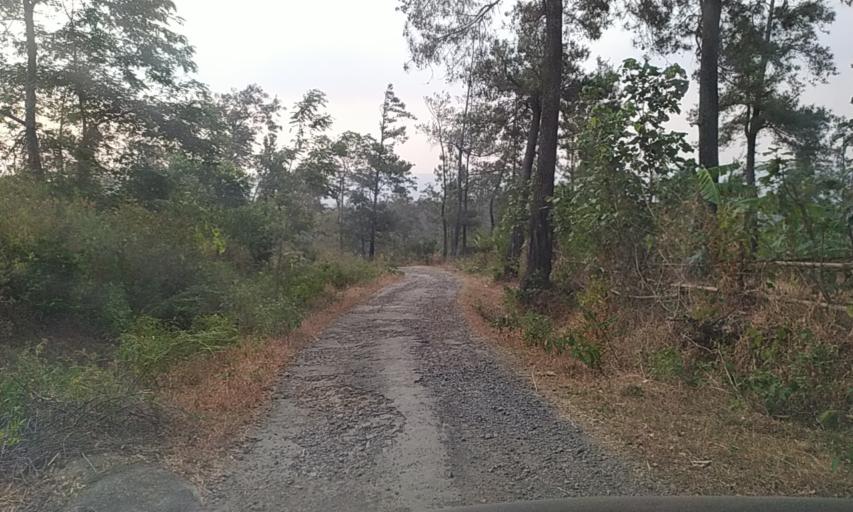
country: ID
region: Central Java
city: Randudongkal
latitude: -7.1369
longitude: 109.3678
